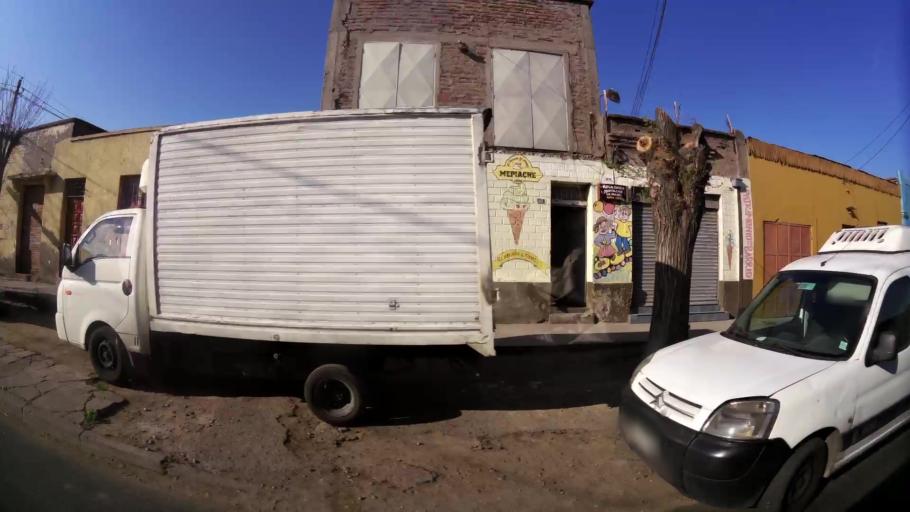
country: CL
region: Santiago Metropolitan
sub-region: Provincia de Santiago
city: Santiago
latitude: -33.4922
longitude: -70.6336
